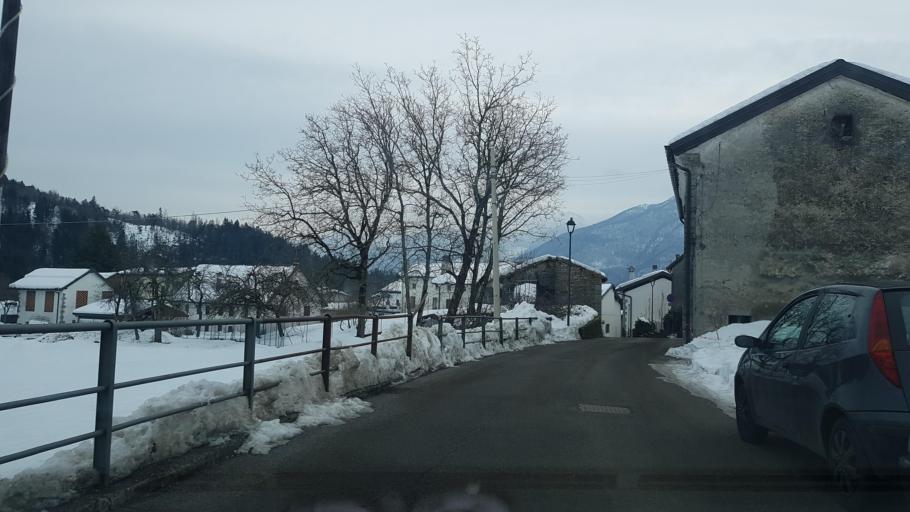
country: IT
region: Friuli Venezia Giulia
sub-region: Provincia di Udine
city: Lauco
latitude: 46.4254
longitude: 12.9322
